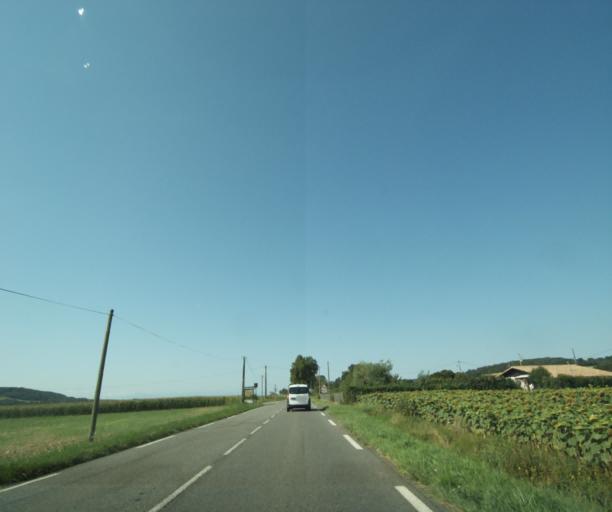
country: FR
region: Midi-Pyrenees
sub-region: Departement de la Haute-Garonne
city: Lagardelle-sur-Leze
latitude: 43.4049
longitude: 1.3698
